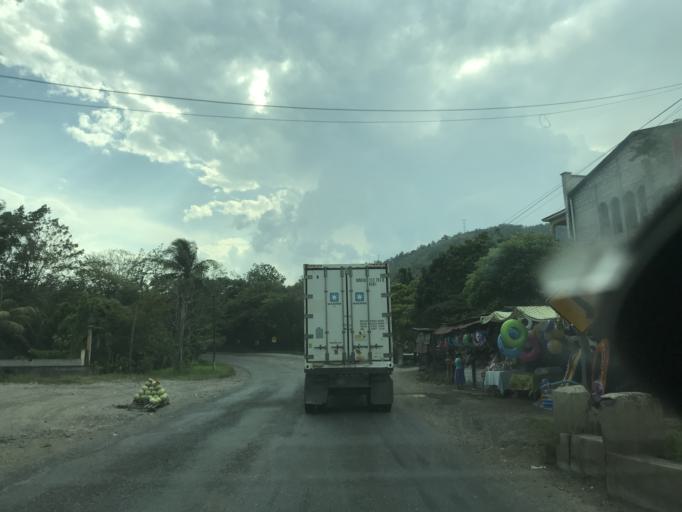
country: GT
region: Zacapa
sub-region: Municipio de Zacapa
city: Gualan
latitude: 15.2074
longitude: -89.2500
